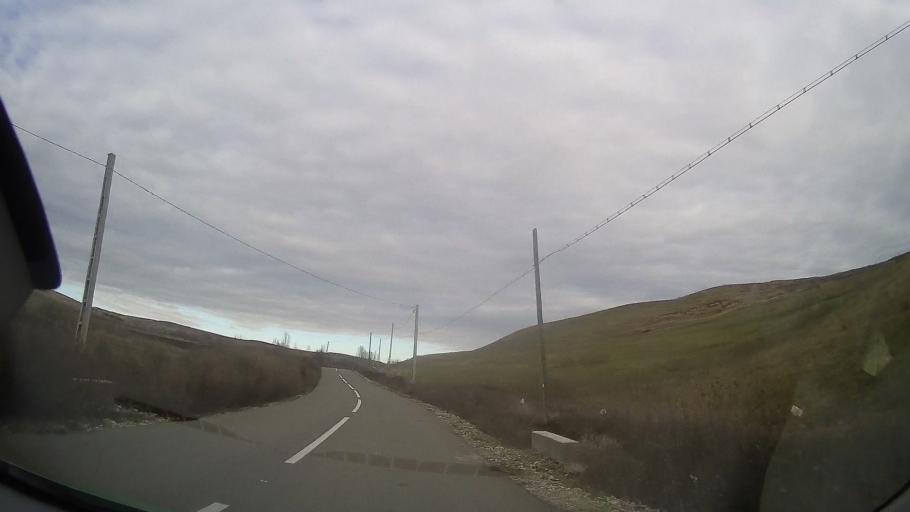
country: RO
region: Bistrita-Nasaud
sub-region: Comuna Silvasu de Campie
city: Silvasu de Campie
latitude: 46.8092
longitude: 24.2949
